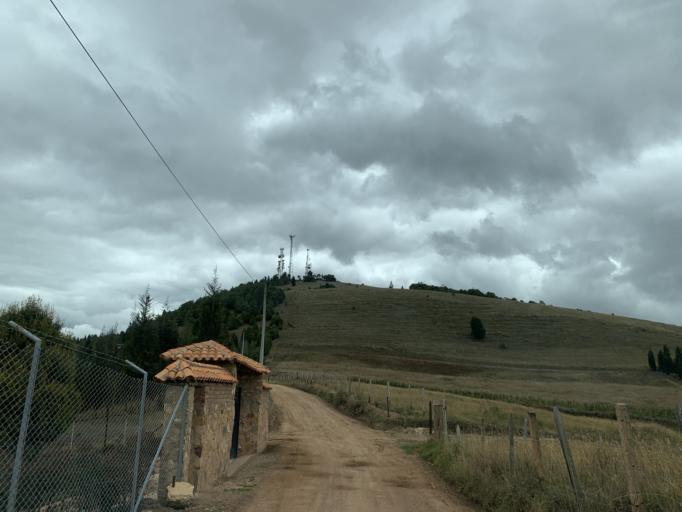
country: CO
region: Boyaca
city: Tunja
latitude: 5.5385
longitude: -73.3201
